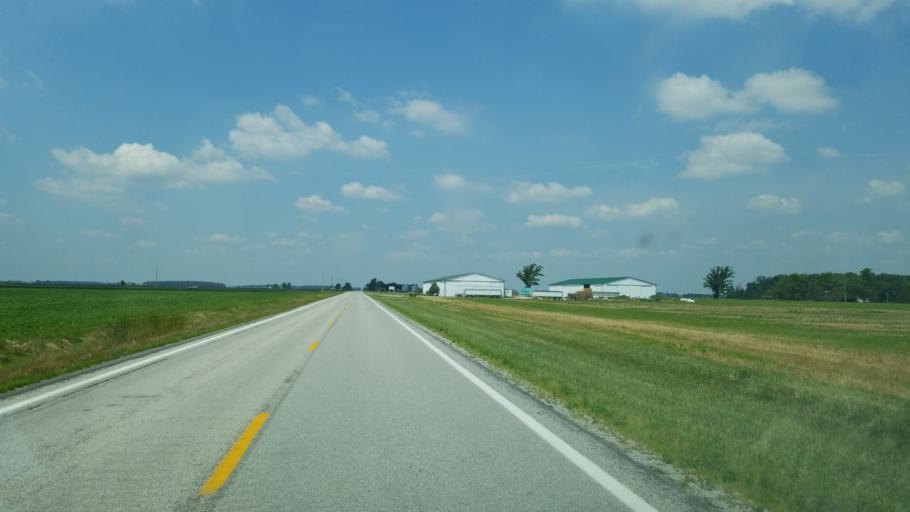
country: US
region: Ohio
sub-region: Henry County
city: Deshler
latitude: 41.2837
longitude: -83.9560
